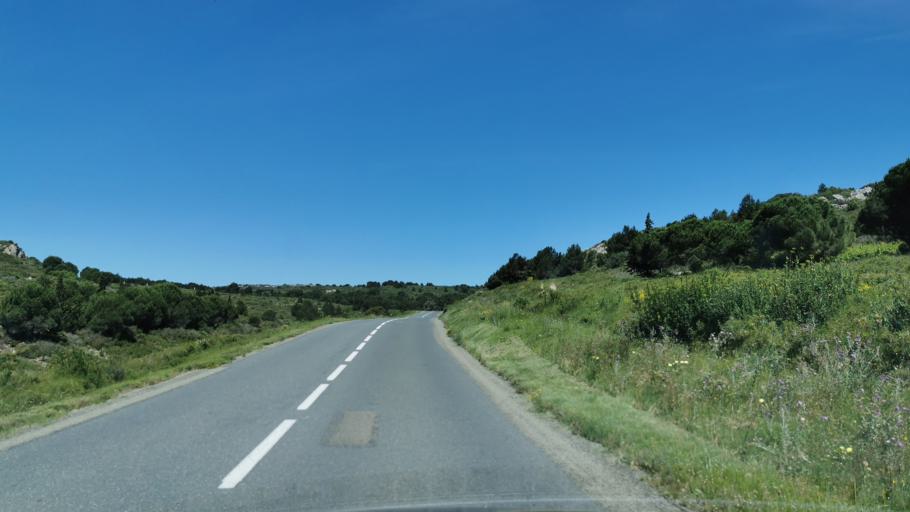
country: FR
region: Languedoc-Roussillon
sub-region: Departement de l'Aude
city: Armissan
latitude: 43.1602
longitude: 3.1477
